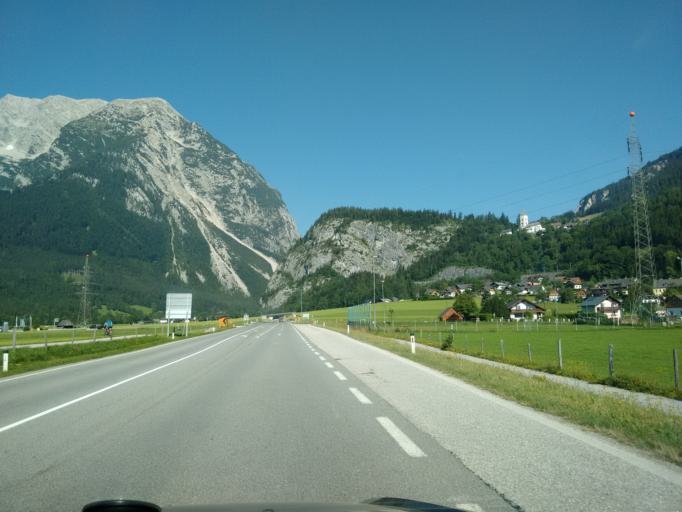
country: AT
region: Styria
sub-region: Politischer Bezirk Liezen
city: Irdning
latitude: 47.5242
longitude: 14.0753
